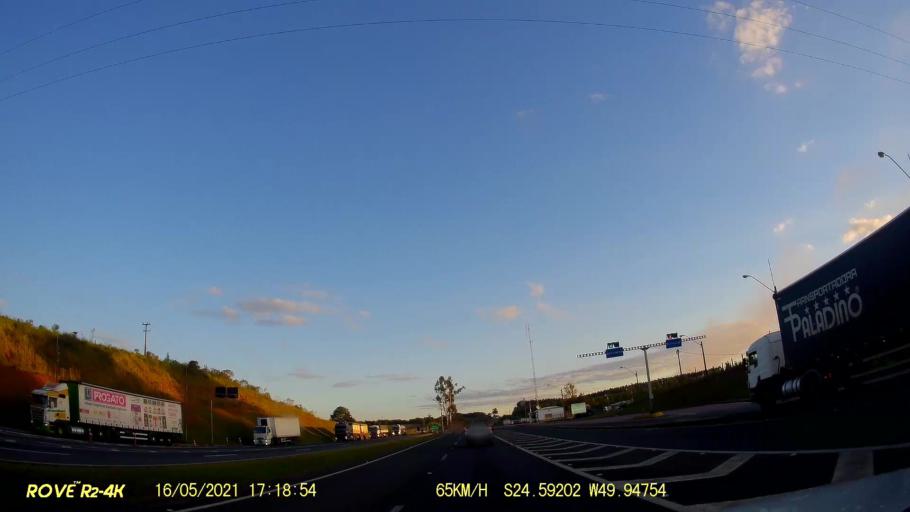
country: BR
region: Parana
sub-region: Pirai Do Sul
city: Pirai do Sul
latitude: -24.5922
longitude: -49.9476
